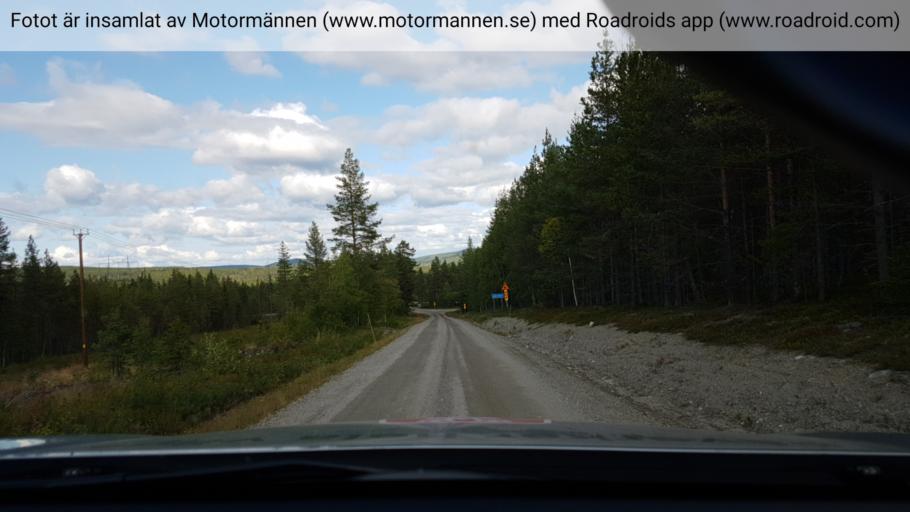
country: SE
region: Vaesterbotten
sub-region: Lycksele Kommun
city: Lycksele
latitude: 64.5562
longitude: 18.9935
